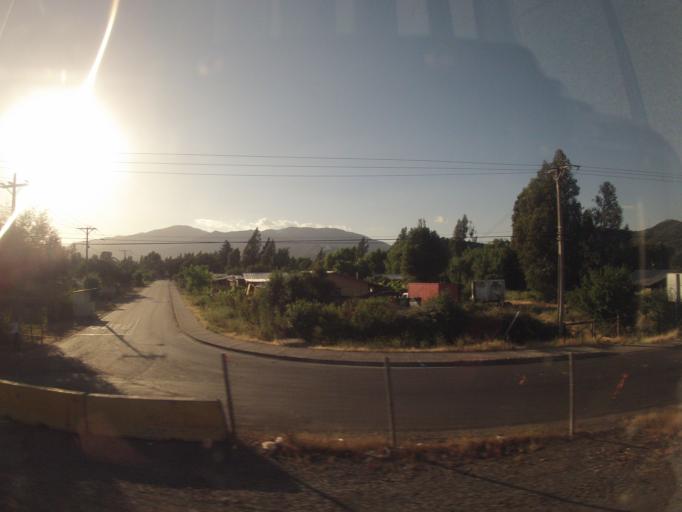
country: CL
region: O'Higgins
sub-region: Provincia de Cachapoal
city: Rengo
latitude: -34.5324
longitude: -70.9398
